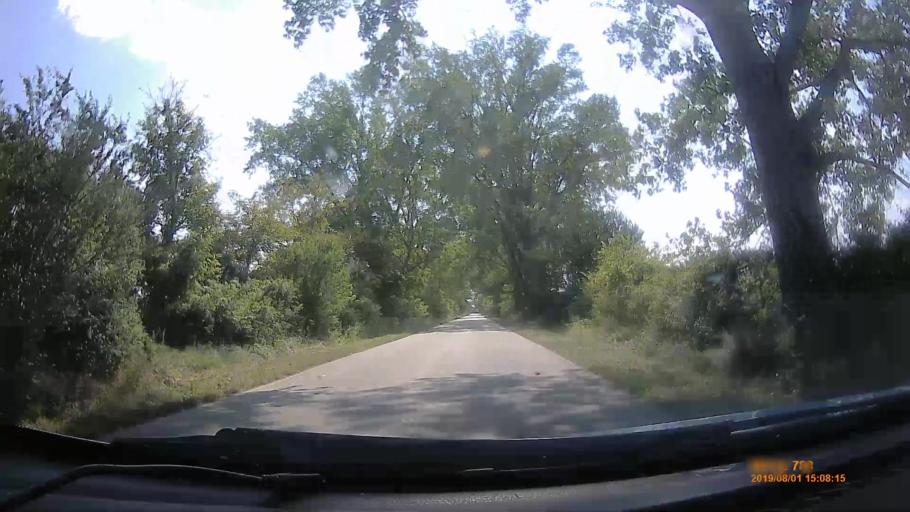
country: HU
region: Baranya
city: Sellye
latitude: 45.8527
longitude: 17.8206
